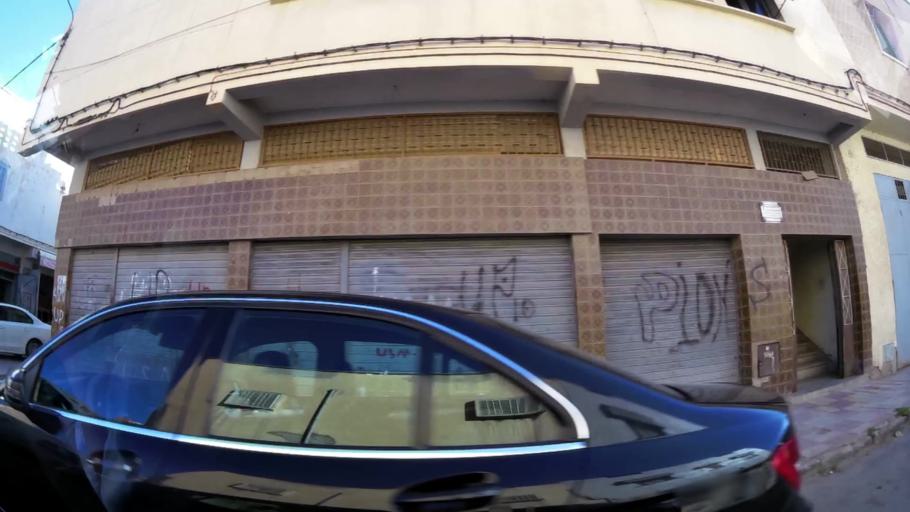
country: MA
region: Oriental
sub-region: Oujda-Angad
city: Oujda
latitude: 34.6871
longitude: -1.9135
